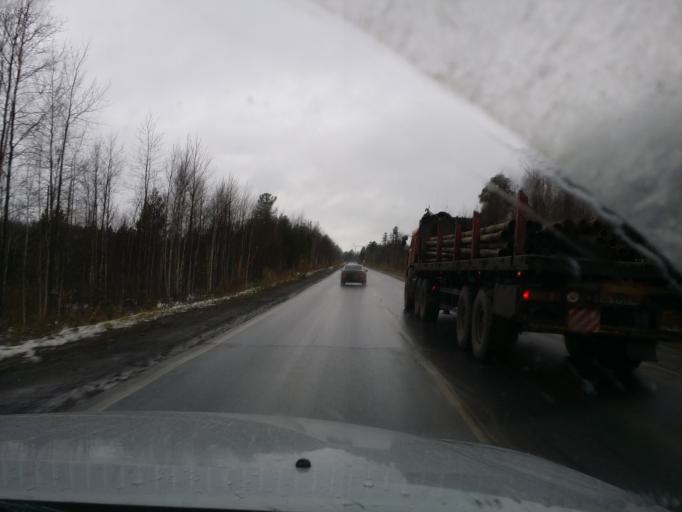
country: RU
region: Khanty-Mansiyskiy Avtonomnyy Okrug
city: Megion
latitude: 61.1620
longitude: 75.7053
